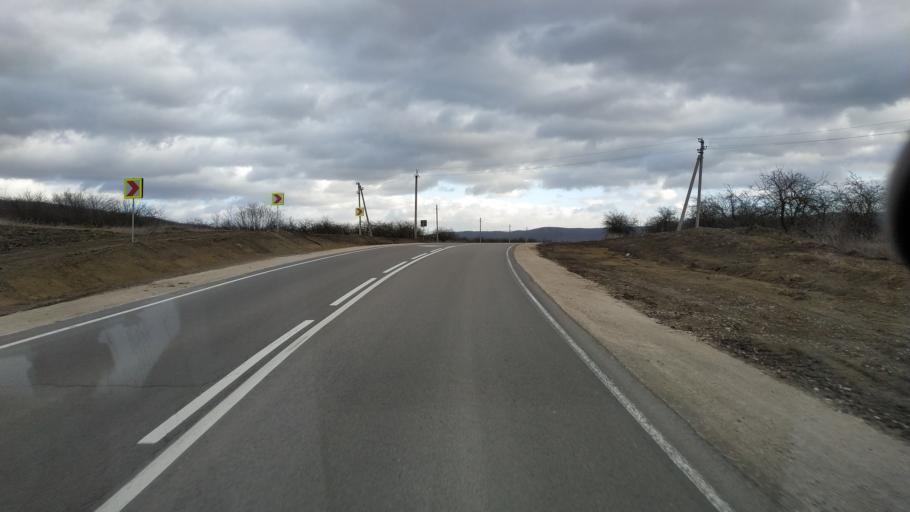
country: MD
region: Calarasi
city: Calarasi
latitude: 47.2700
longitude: 28.2261
